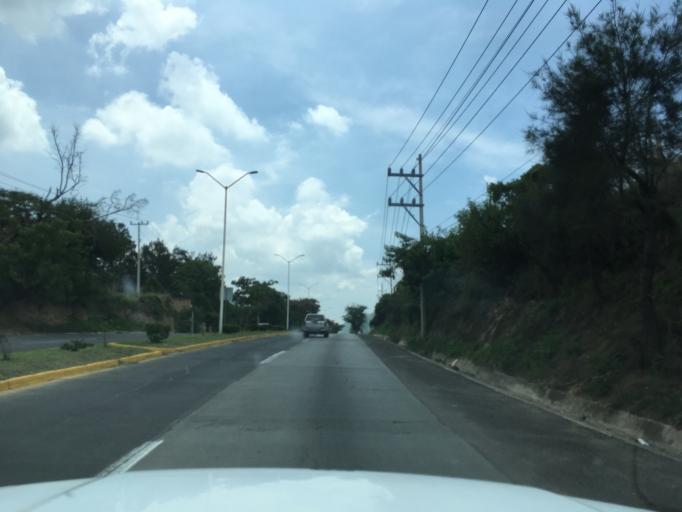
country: MX
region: Jalisco
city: Tlajomulco de Zuniga
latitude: 20.4894
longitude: -103.4642
